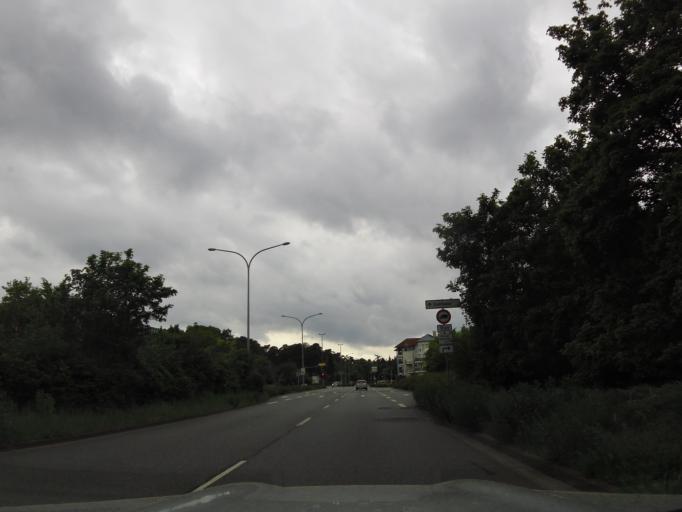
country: DE
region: Hesse
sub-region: Regierungsbezirk Darmstadt
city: Russelsheim
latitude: 49.9876
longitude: 8.4435
